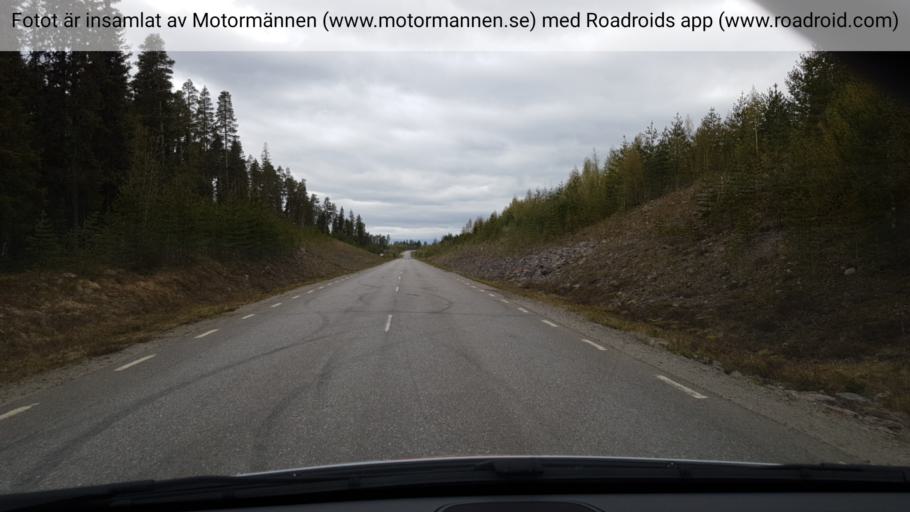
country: SE
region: Vaesterbotten
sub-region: Sorsele Kommun
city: Sorsele
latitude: 65.5503
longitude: 17.4833
